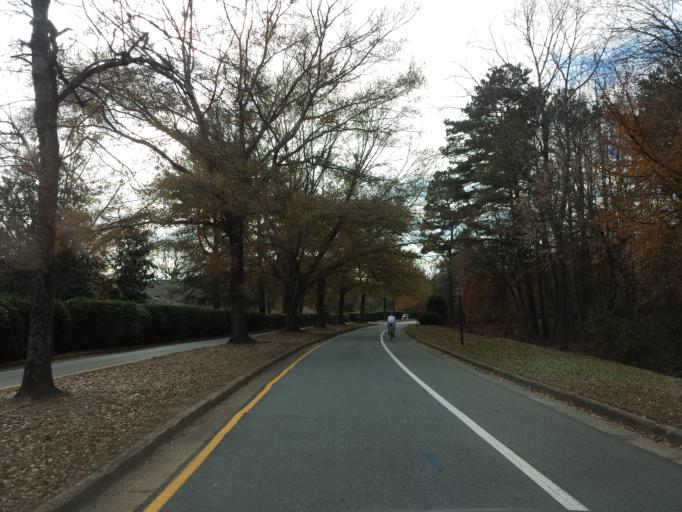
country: US
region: Georgia
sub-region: Fulton County
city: Sandy Springs
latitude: 33.9256
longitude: -84.4316
